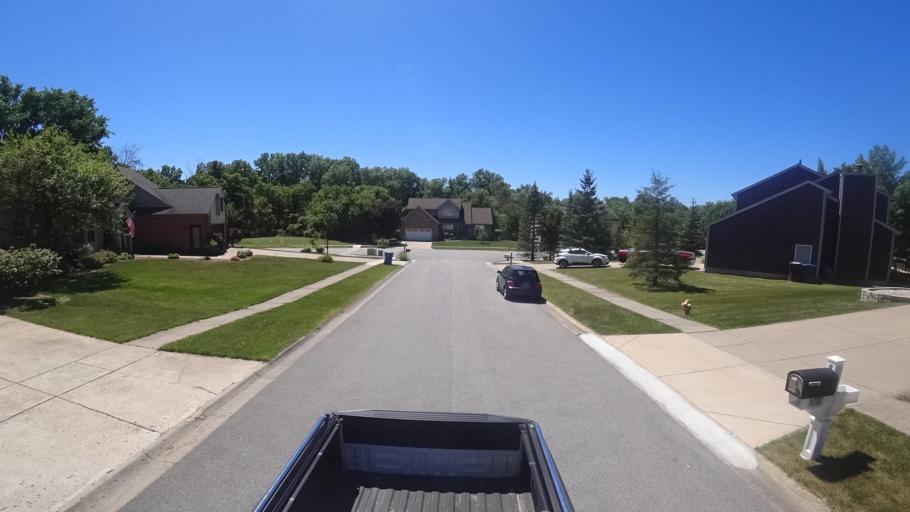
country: US
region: Indiana
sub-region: Porter County
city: Porter
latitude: 41.6291
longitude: -87.0708
